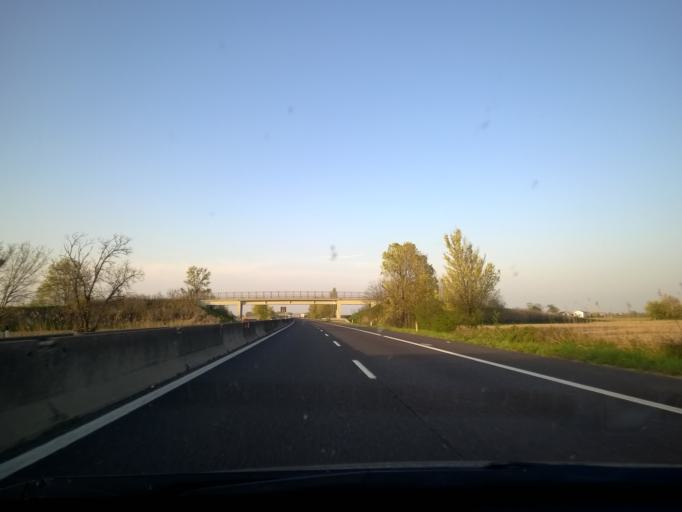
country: IT
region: Emilia-Romagna
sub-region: Provincia di Bologna
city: Malalbergo
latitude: 44.7466
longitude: 11.5269
